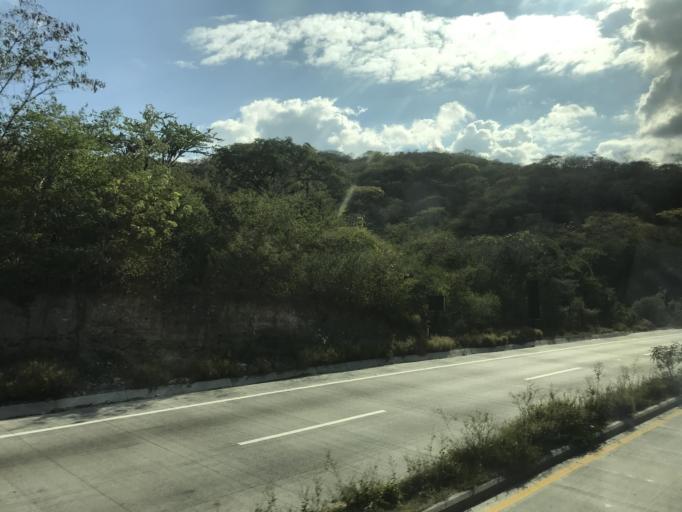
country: GT
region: El Progreso
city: Guastatoya
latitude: 14.8544
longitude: -90.0928
